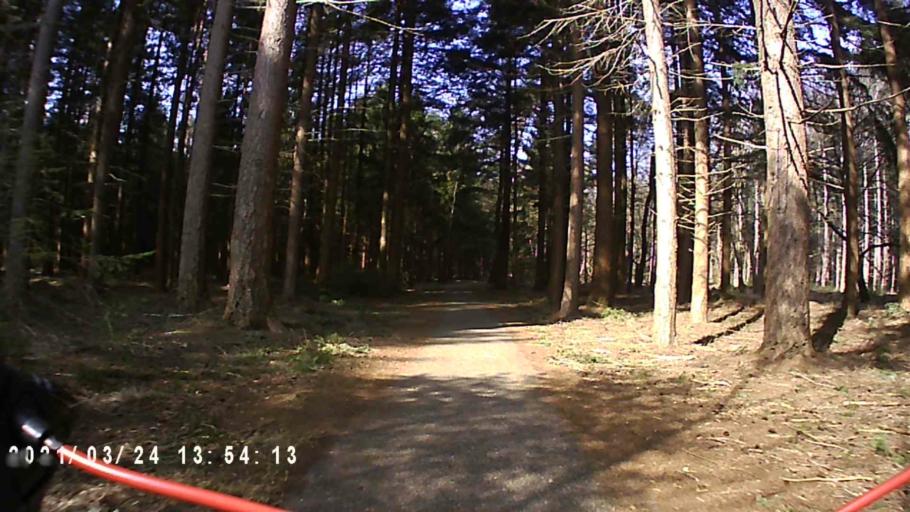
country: NL
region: Friesland
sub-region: Gemeente Smallingerland
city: Drachtstercompagnie
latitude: 53.0800
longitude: 6.2387
